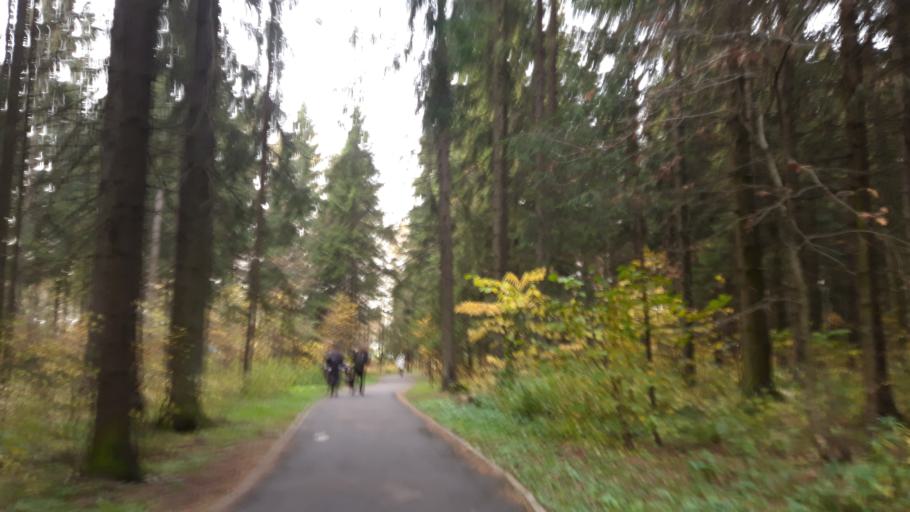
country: RU
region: Moscow
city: Zelenograd
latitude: 55.9985
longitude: 37.1650
